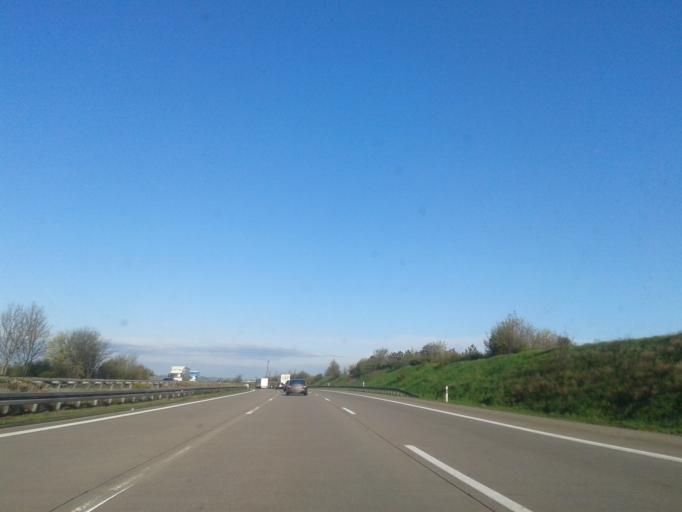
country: DE
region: Saxony
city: Klipphausen
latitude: 51.0606
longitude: 13.4561
